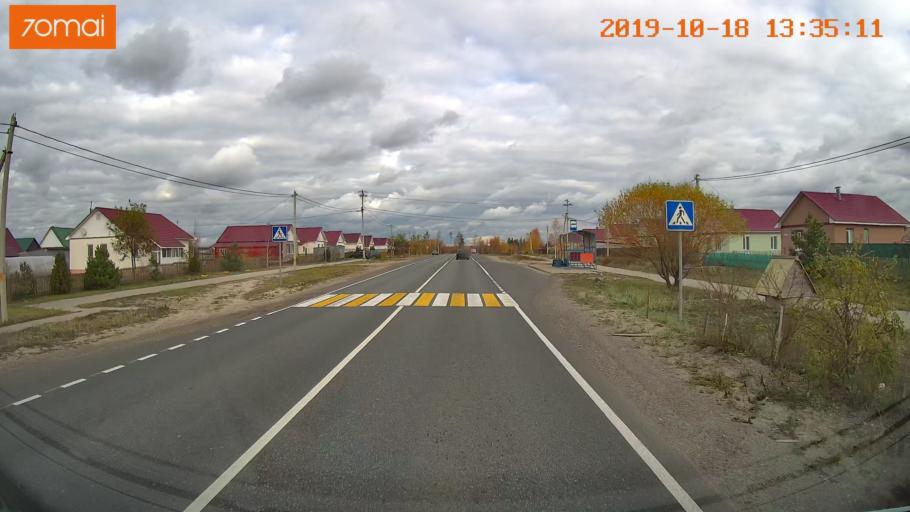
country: RU
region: Rjazan
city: Solotcha
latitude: 54.8597
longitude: 39.9644
